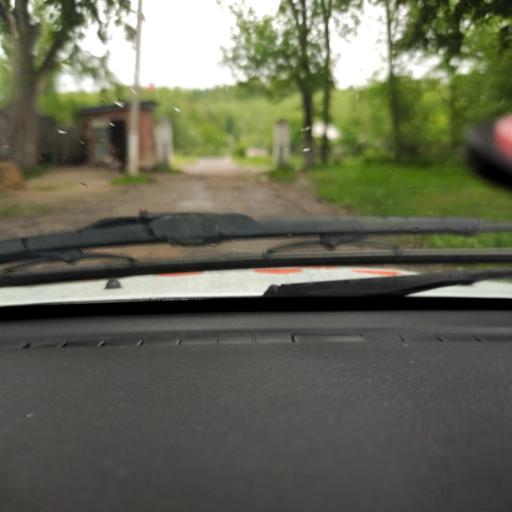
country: RU
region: Voronezj
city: Devitsa
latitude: 51.6060
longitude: 39.0011
